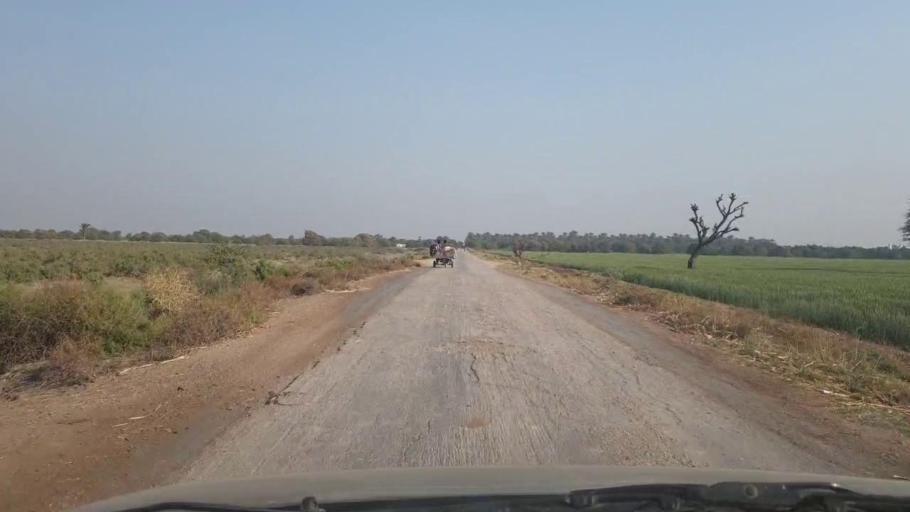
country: PK
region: Sindh
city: Digri
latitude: 25.2628
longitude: 69.1726
